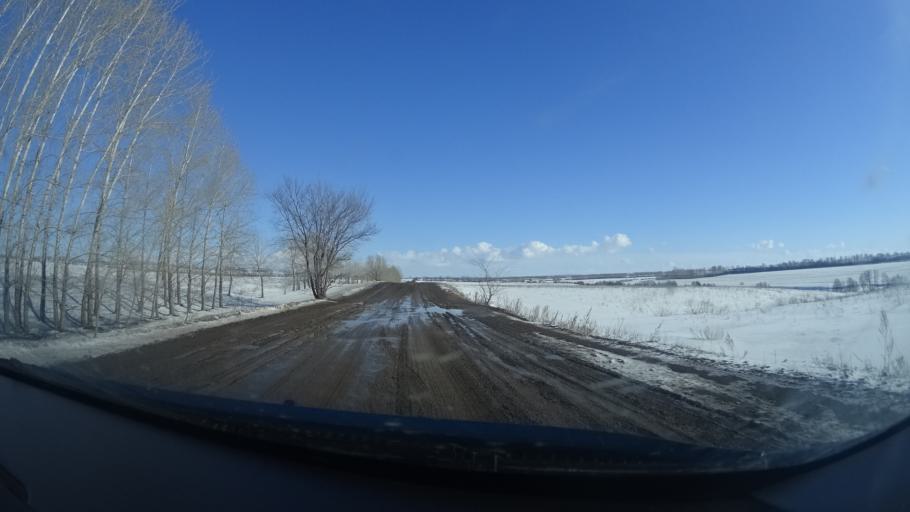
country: RU
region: Bashkortostan
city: Chishmy
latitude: 54.6013
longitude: 55.2228
